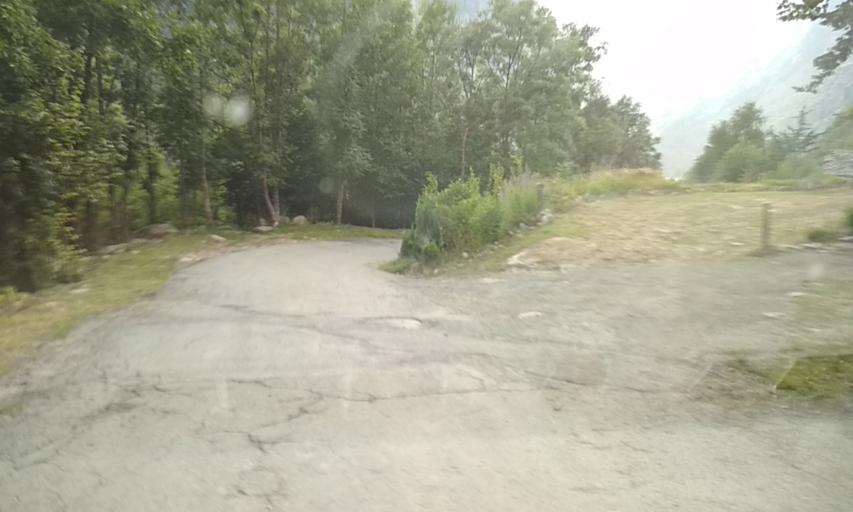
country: IT
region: Piedmont
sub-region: Provincia di Torino
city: Noasca
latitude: 45.4564
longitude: 7.3054
